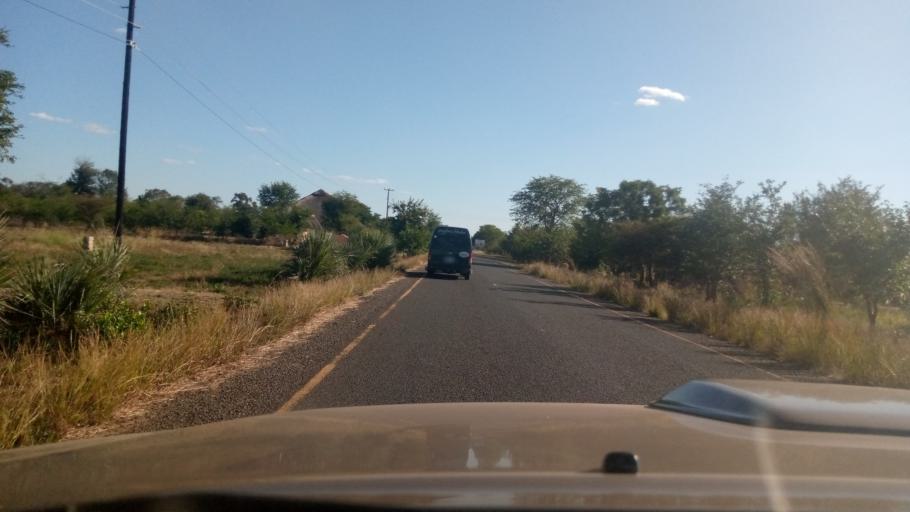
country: ZM
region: Southern
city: Livingstone
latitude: -17.8795
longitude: 25.8492
